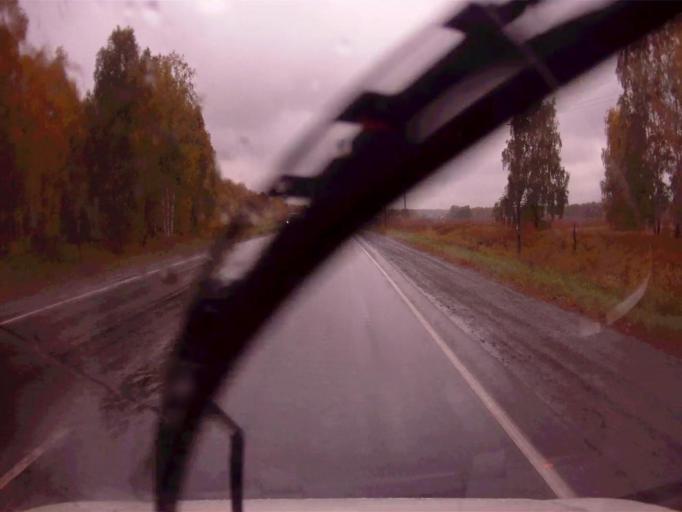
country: RU
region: Chelyabinsk
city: Argayash
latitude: 55.4026
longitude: 61.0681
